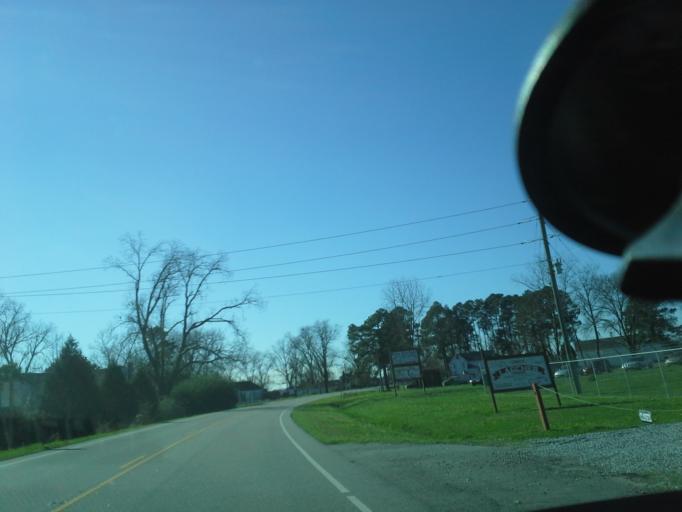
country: US
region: North Carolina
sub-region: Beaufort County
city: Belhaven
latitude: 35.5292
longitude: -76.7389
